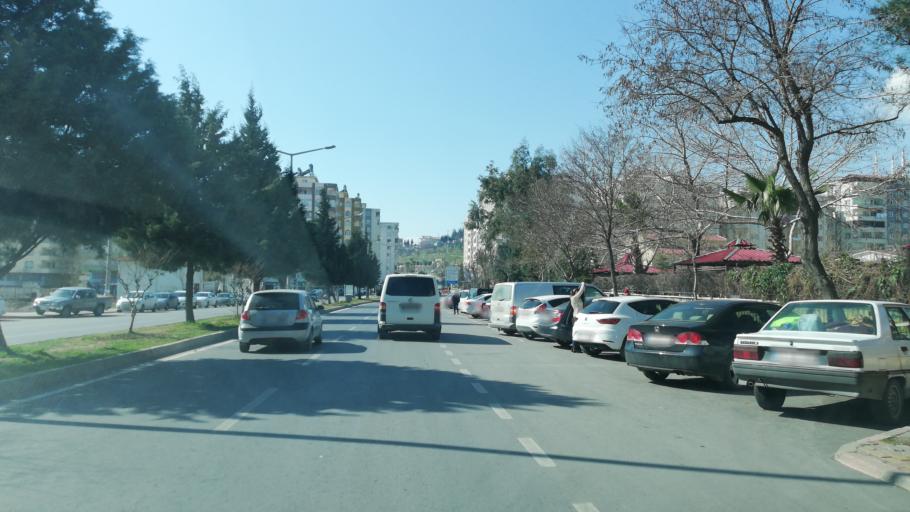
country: TR
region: Kahramanmaras
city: Kahramanmaras
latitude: 37.5713
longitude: 36.9217
